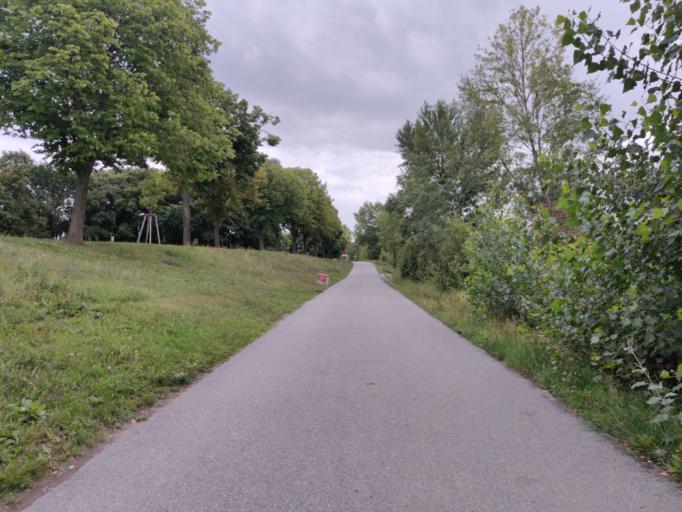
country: AT
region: Vienna
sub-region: Wien Stadt
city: Vienna
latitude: 48.2411
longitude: 16.3934
